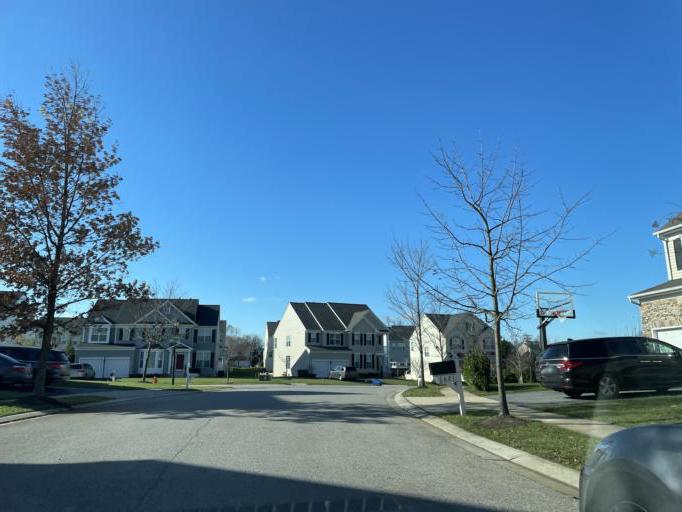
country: US
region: Maryland
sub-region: Baltimore County
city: Pikesville
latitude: 39.3749
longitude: -76.6698
